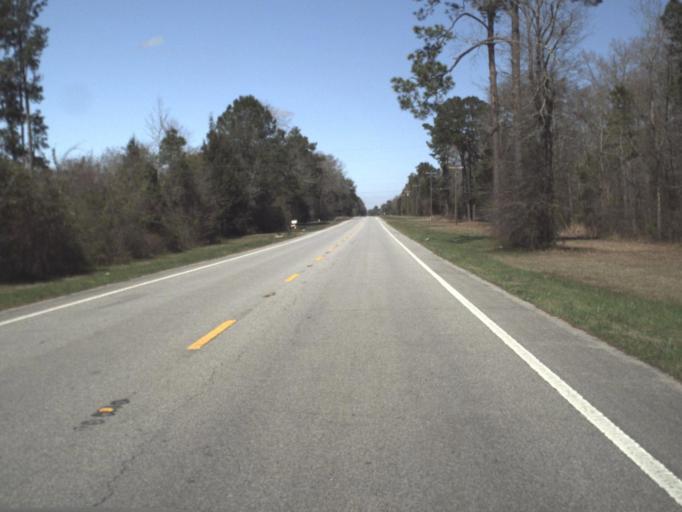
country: US
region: Florida
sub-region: Gadsden County
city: Gretna
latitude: 30.6842
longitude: -84.6201
